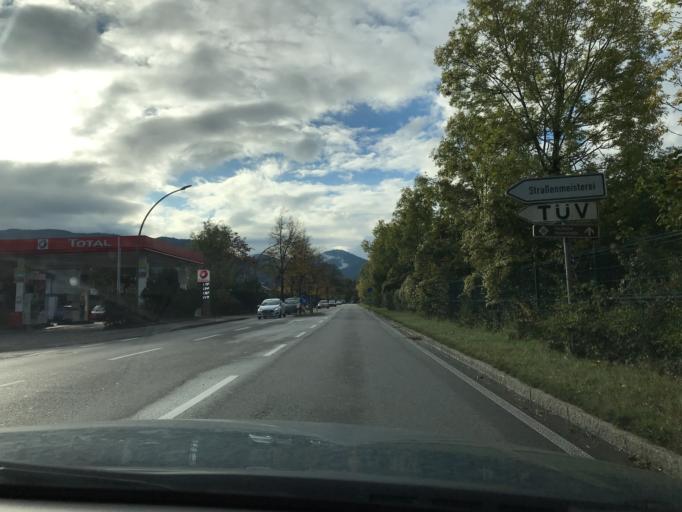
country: DE
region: Bavaria
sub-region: Upper Bavaria
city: Bad Toelz
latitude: 47.7483
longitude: 11.5649
